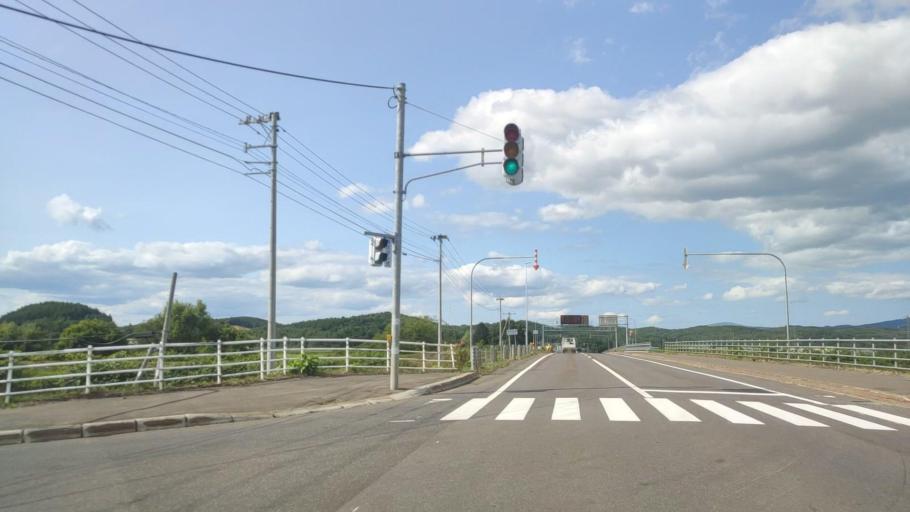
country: JP
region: Hokkaido
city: Nayoro
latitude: 44.3714
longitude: 142.4361
